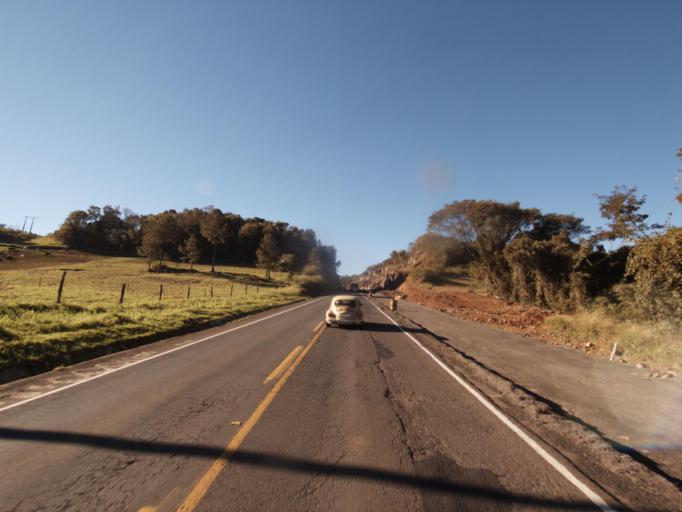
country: AR
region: Misiones
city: Bernardo de Irigoyen
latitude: -26.5758
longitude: -53.5129
